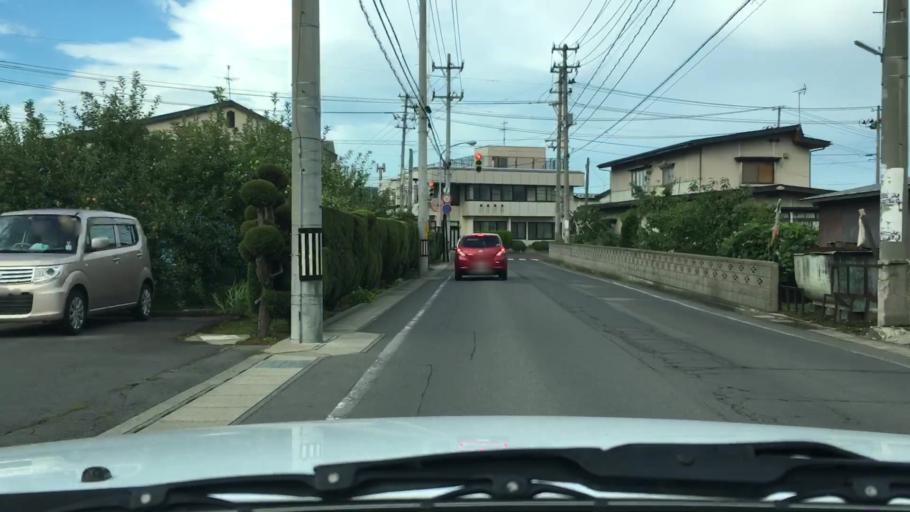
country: JP
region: Aomori
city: Hirosaki
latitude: 40.5862
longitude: 140.4618
